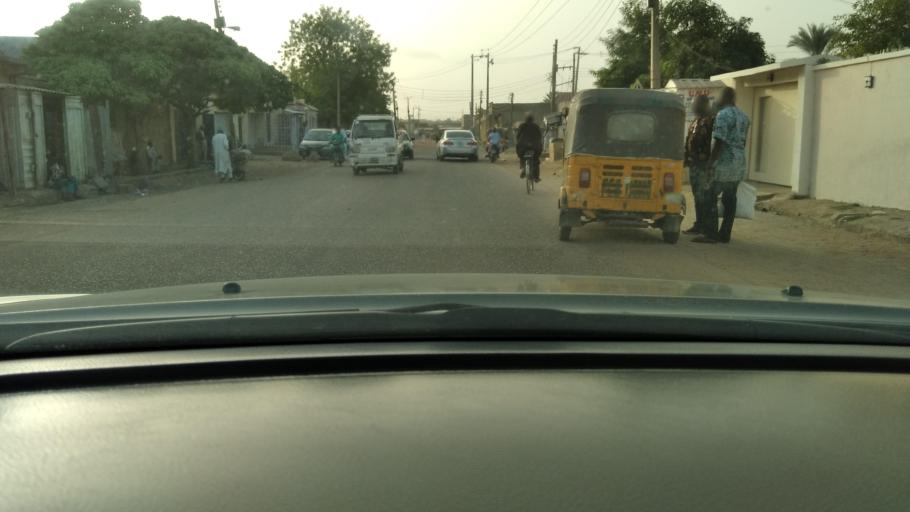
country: NG
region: Kano
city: Kano
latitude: 11.9572
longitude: 8.5225
